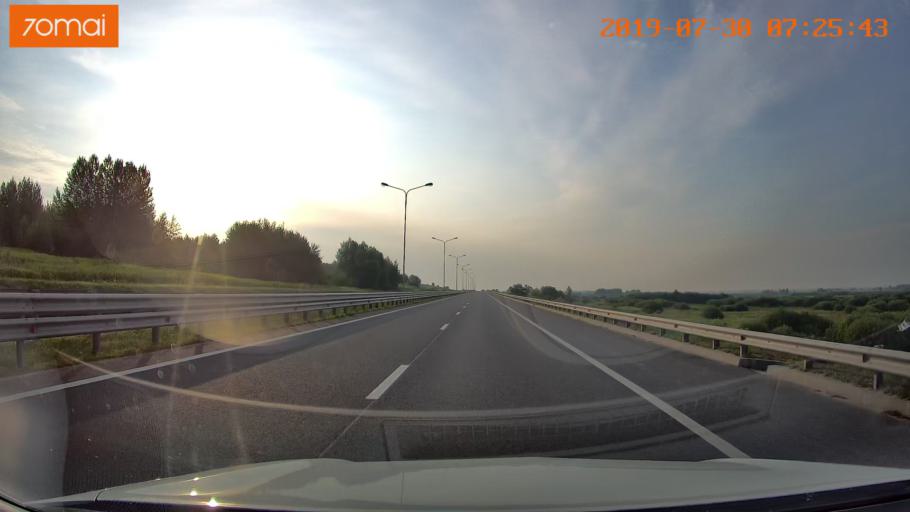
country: RU
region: Kaliningrad
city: Gvardeysk
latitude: 54.6854
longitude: 20.8411
